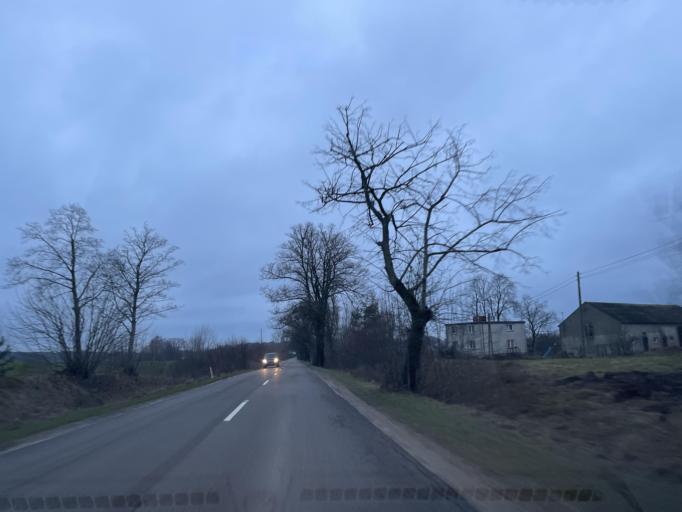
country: PL
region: Pomeranian Voivodeship
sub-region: Powiat kartuski
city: Kartuzy
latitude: 54.4098
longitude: 18.2096
